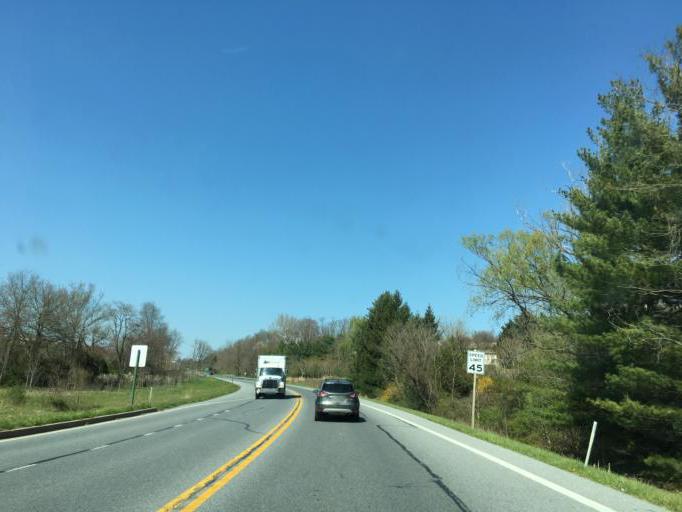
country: US
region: Maryland
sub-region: Carroll County
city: Westminster
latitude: 39.5768
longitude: -77.0116
